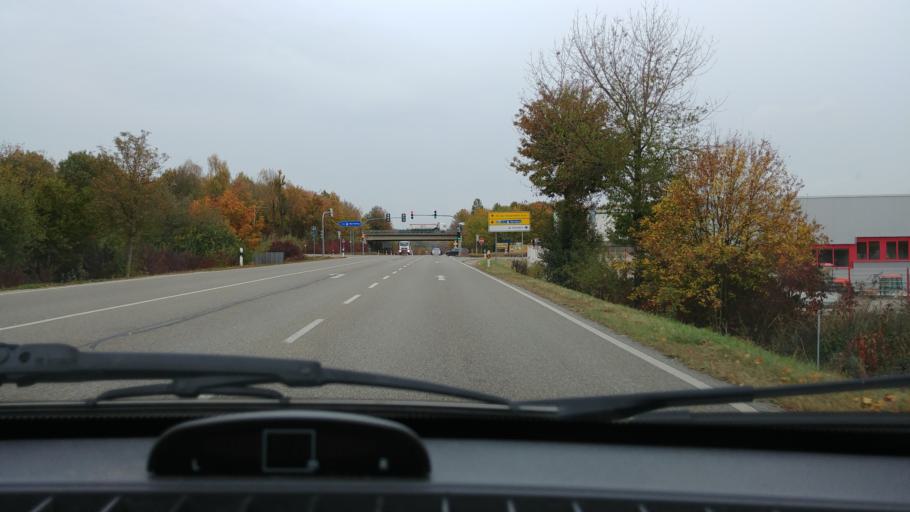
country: DE
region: Baden-Wuerttemberg
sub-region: Regierungsbezirk Stuttgart
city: Satteldorf
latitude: 49.1812
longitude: 10.0711
